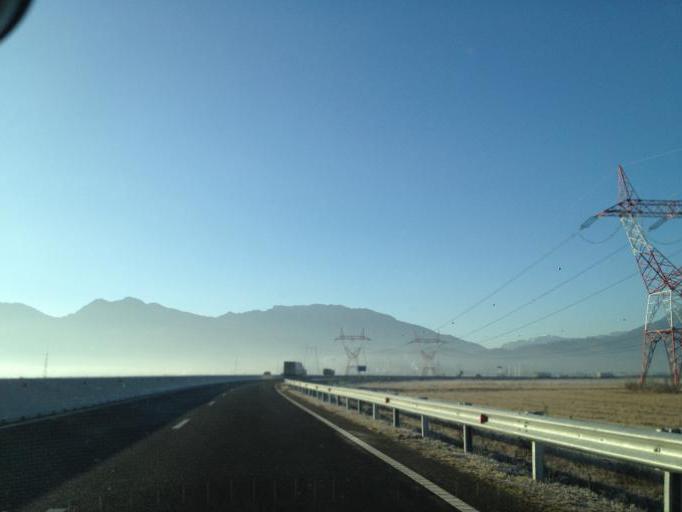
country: RO
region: Brasov
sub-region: Municipiul Sacele
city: Sacele
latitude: 45.6415
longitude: 25.6629
